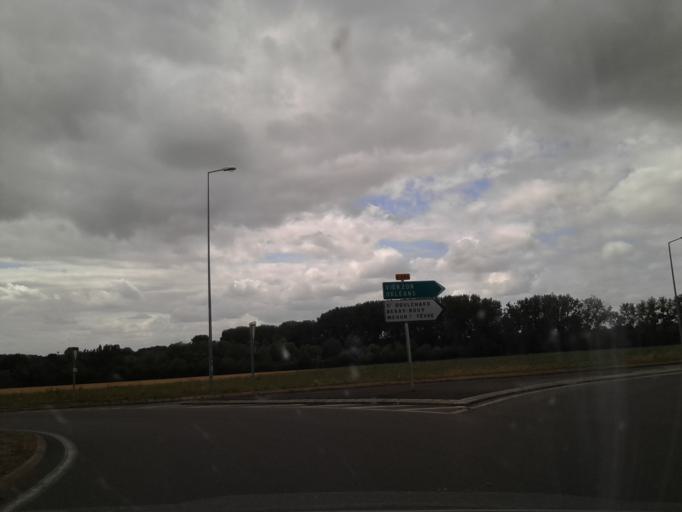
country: FR
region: Centre
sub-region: Departement du Cher
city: Saint-Doulchard
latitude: 47.0820
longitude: 2.3542
